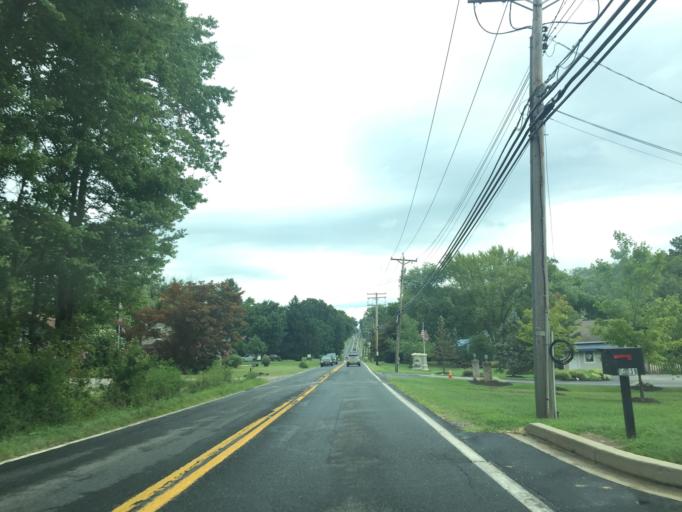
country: US
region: Maryland
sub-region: Baltimore County
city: White Marsh
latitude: 39.3859
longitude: -76.4305
